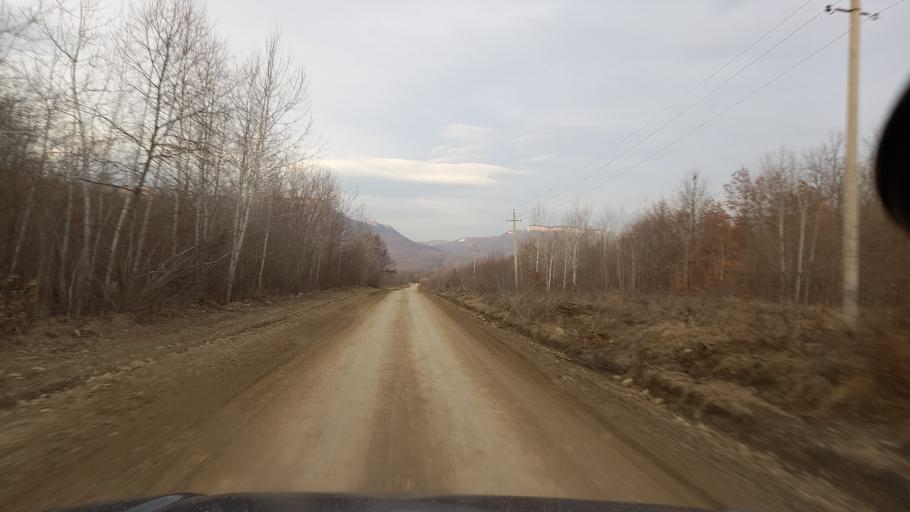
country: RU
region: Adygeya
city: Kamennomostskiy
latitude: 44.1796
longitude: 40.2582
